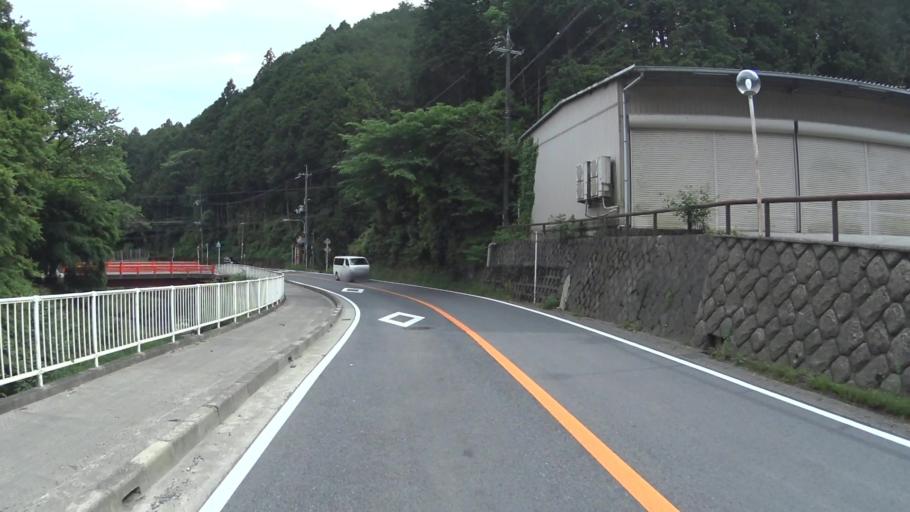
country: JP
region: Shiga Prefecture
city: Kitahama
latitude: 35.1604
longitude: 135.8656
